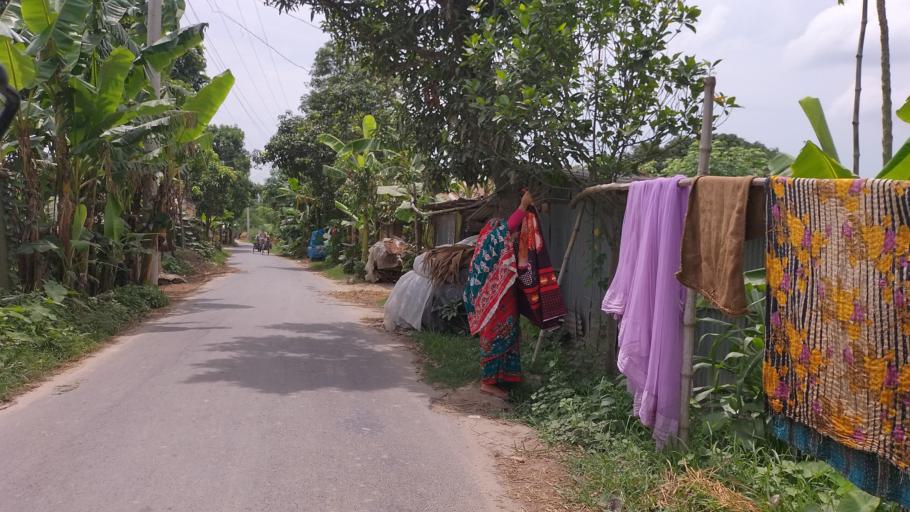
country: BD
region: Rajshahi
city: Rajshahi
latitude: 24.5155
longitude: 88.6277
